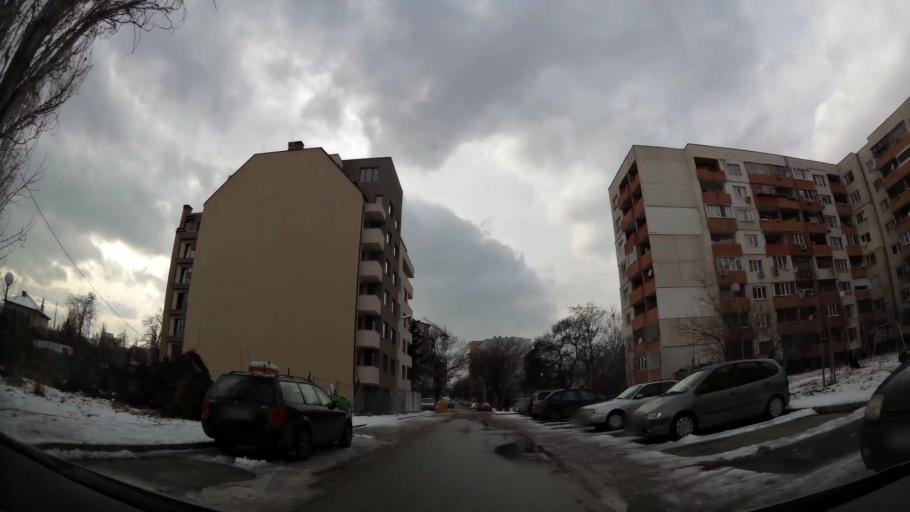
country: BG
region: Sofia-Capital
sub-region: Stolichna Obshtina
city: Sofia
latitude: 42.7001
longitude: 23.3573
